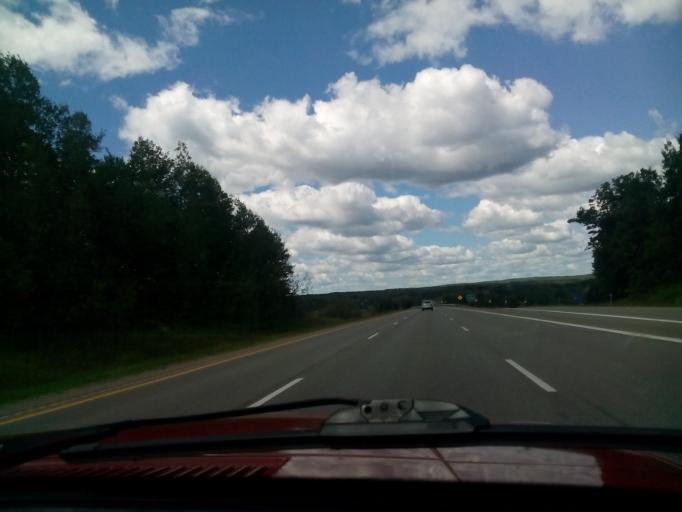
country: US
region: Michigan
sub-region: Ogemaw County
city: West Branch
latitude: 44.2712
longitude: -84.2755
